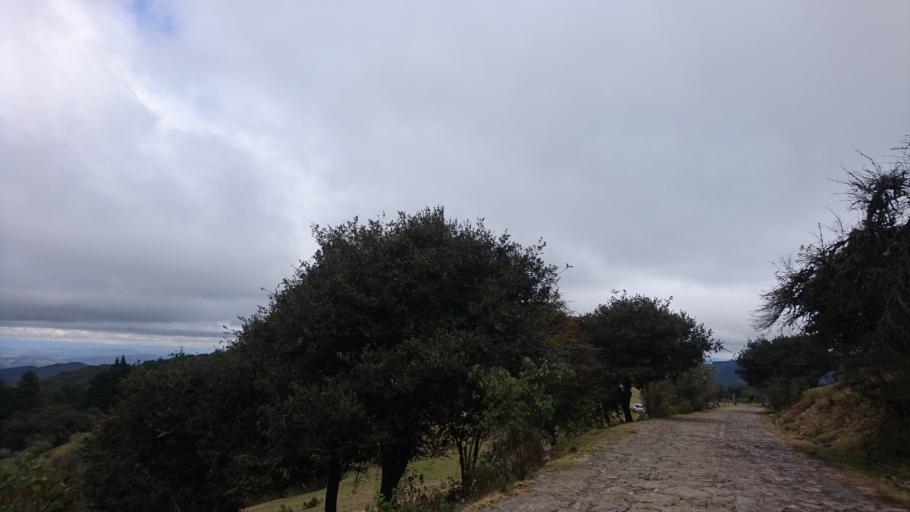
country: MX
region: San Luis Potosi
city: Zaragoza
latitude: 22.0735
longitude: -100.6385
